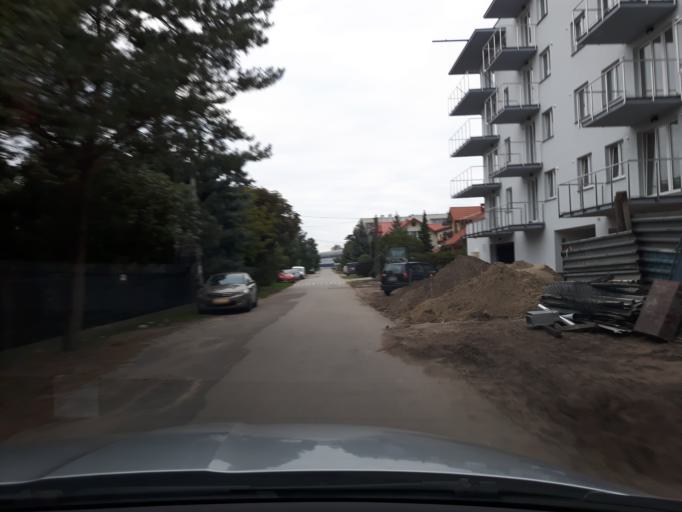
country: PL
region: Masovian Voivodeship
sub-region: Powiat wolominski
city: Zabki
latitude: 52.3056
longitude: 21.0965
